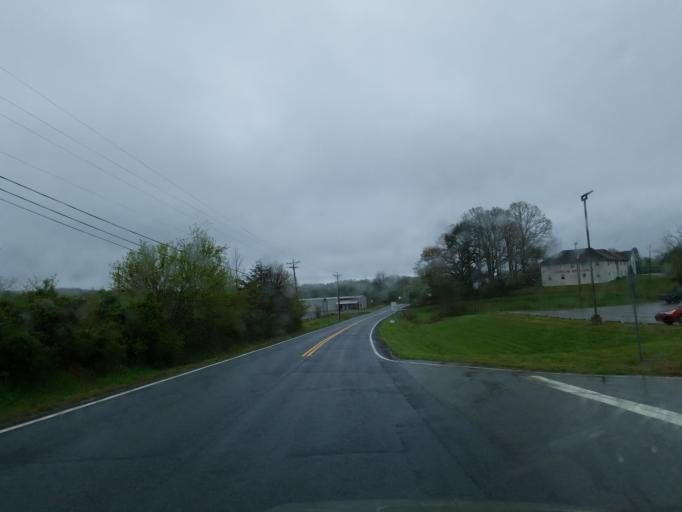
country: US
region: Georgia
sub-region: Fannin County
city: Blue Ridge
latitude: 34.8794
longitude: -84.2467
